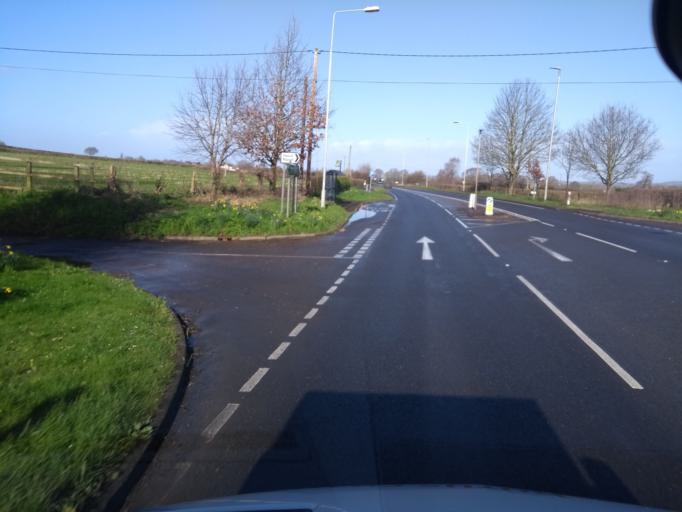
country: GB
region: England
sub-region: Somerset
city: Yeovil
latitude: 50.9673
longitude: -2.6563
